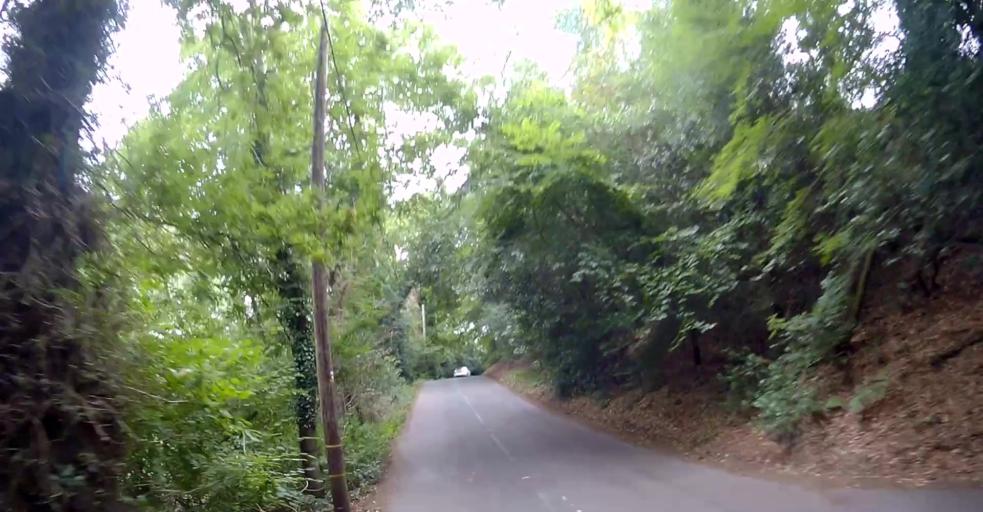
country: GB
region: England
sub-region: Surrey
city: Hale
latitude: 51.2123
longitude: -0.7722
